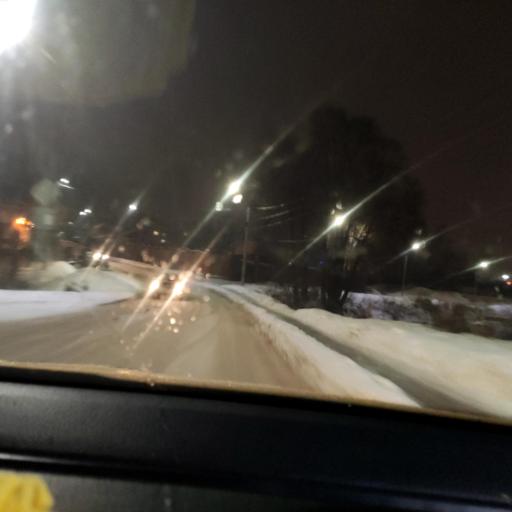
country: RU
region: Moskovskaya
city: Rozhdestveno
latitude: 55.8093
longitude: 37.0066
